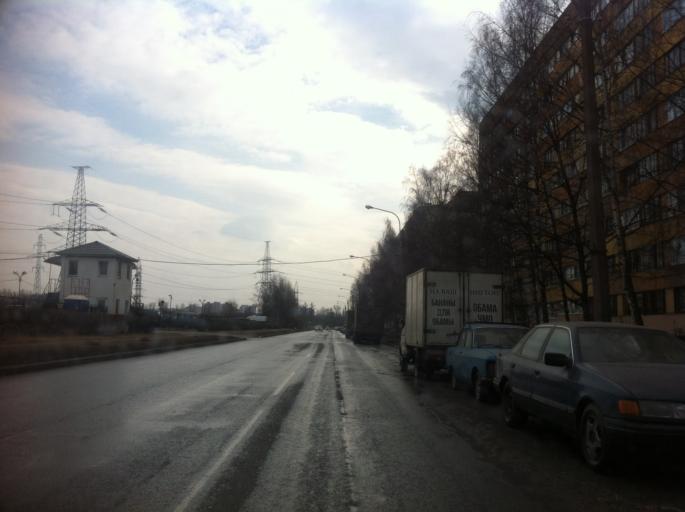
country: RU
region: St.-Petersburg
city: Uritsk
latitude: 59.8498
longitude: 30.1940
